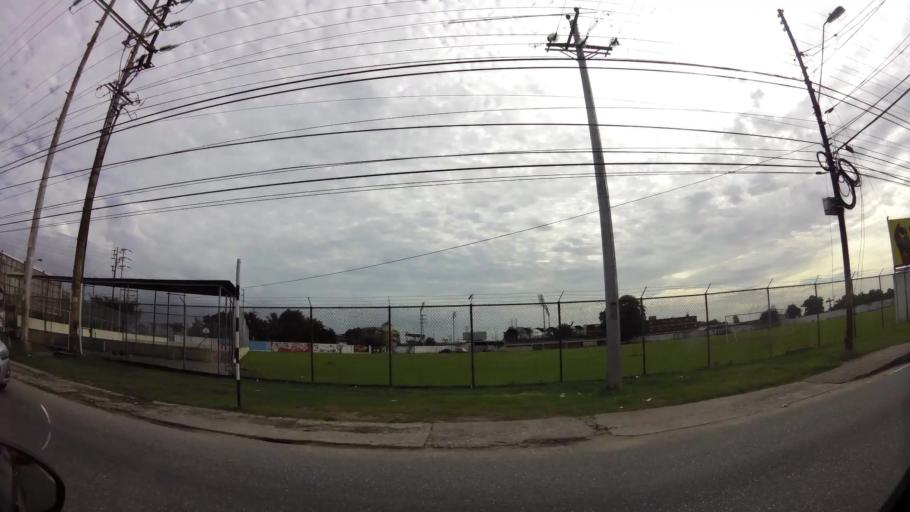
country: TT
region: City of Port of Spain
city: Mucurapo
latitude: 10.6665
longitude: -61.5309
